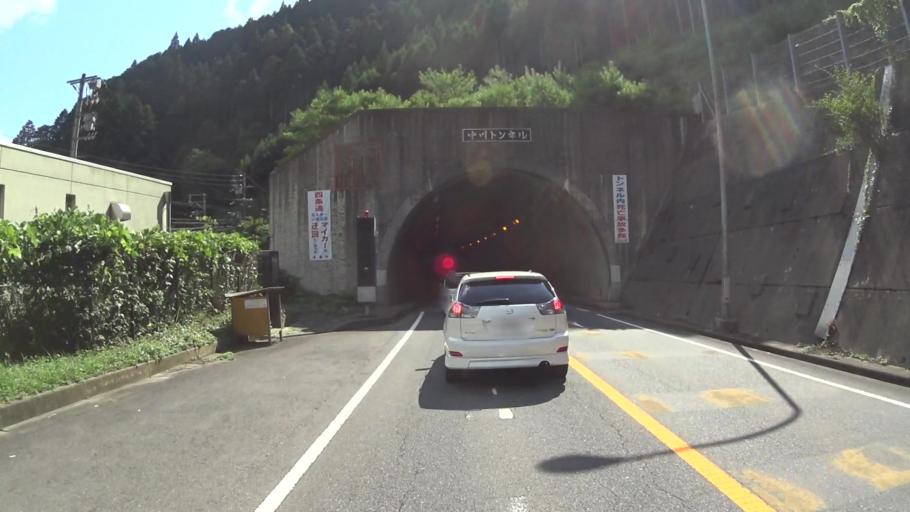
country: JP
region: Kyoto
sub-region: Kyoto-shi
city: Kamigyo-ku
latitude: 35.0947
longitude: 135.6888
